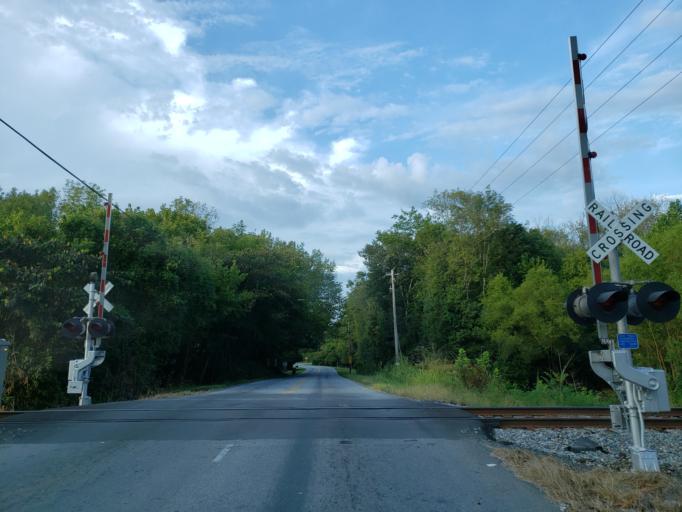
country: US
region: Georgia
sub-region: Bartow County
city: Cartersville
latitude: 34.2165
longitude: -84.8463
